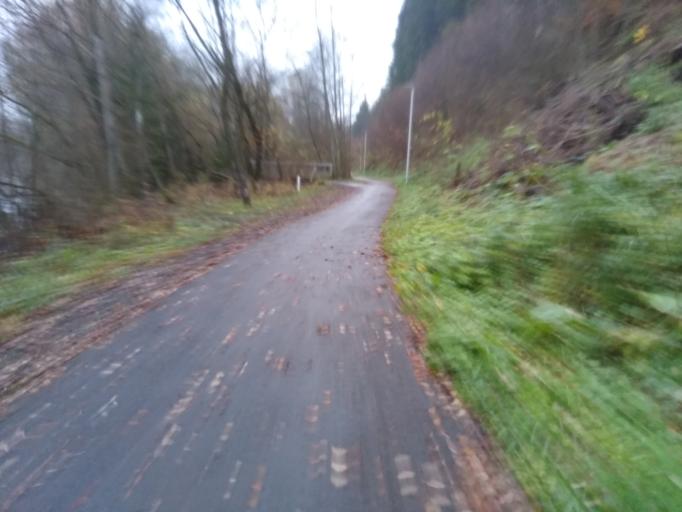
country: AT
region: Styria
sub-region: Politischer Bezirk Bruck-Muerzzuschlag
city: Kapfenberg
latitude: 47.4446
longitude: 15.3102
